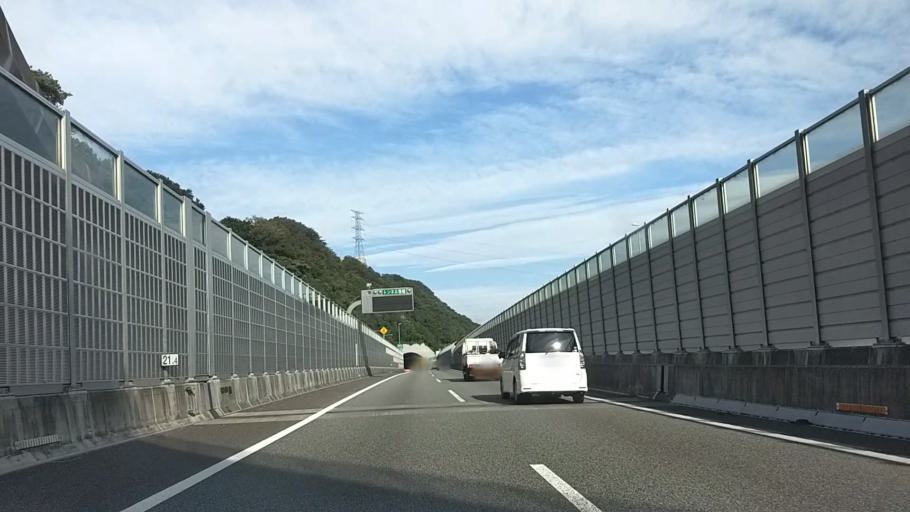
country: JP
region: Kanagawa
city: Zama
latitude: 35.5232
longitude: 139.3537
